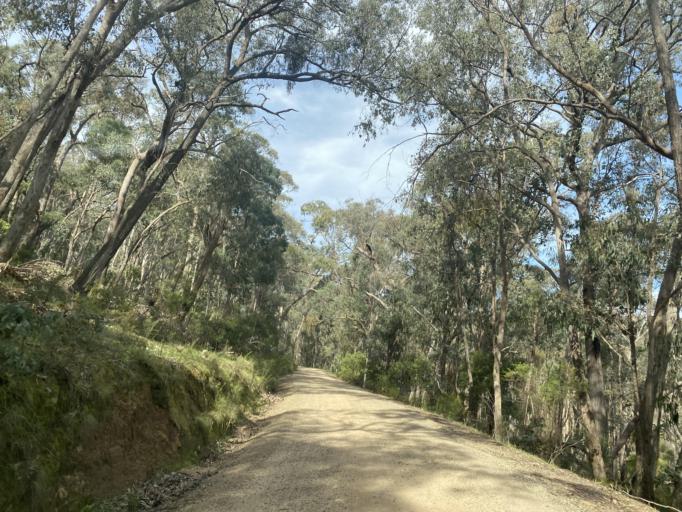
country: AU
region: Victoria
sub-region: Mansfield
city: Mansfield
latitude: -36.8272
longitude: 146.1545
